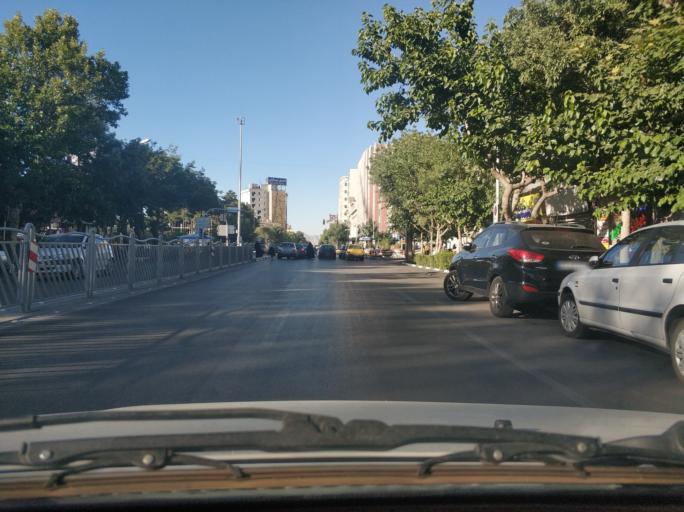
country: IR
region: Razavi Khorasan
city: Mashhad
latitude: 36.2933
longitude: 59.6096
